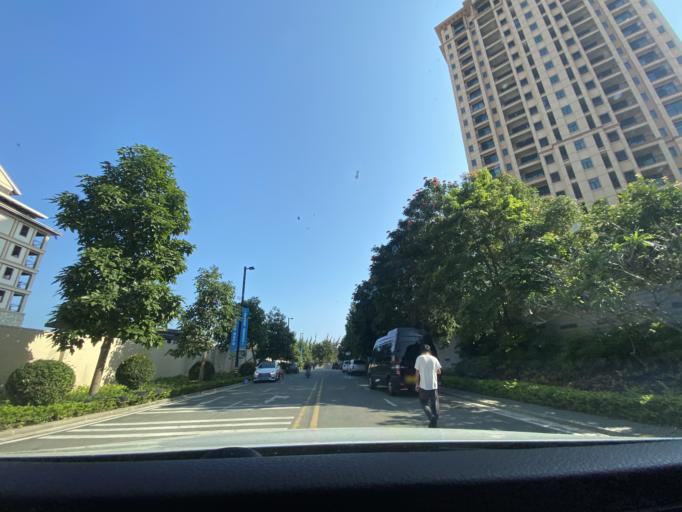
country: CN
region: Hainan
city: Yingzhou
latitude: 18.4086
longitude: 109.8810
